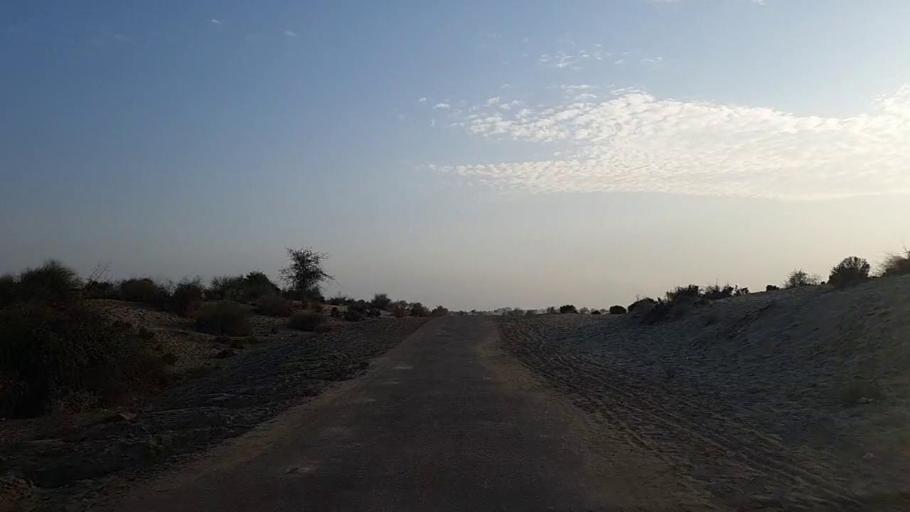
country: PK
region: Sindh
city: Jam Sahib
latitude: 26.3953
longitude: 68.5010
